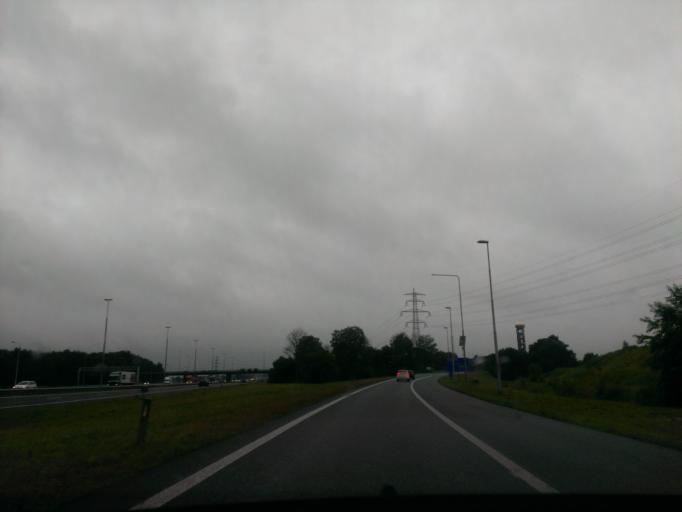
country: NL
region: Gelderland
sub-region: Gemeente Apeldoorn
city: Apeldoorn
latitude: 52.2102
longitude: 6.0218
